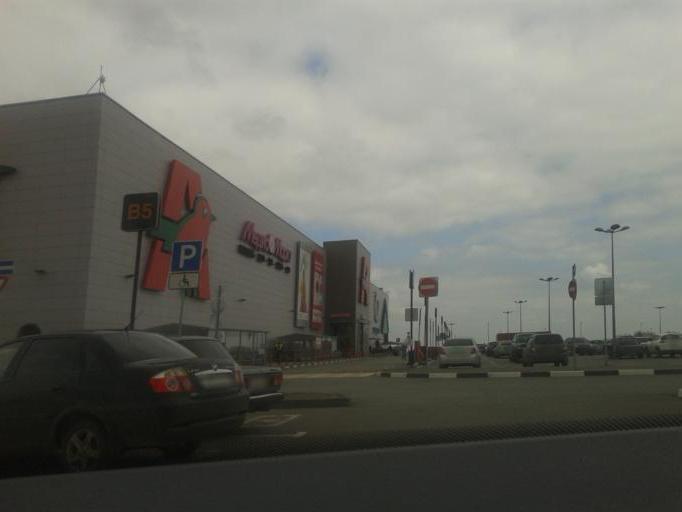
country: RU
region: Volgograd
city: Volgograd
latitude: 48.6353
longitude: 44.4342
